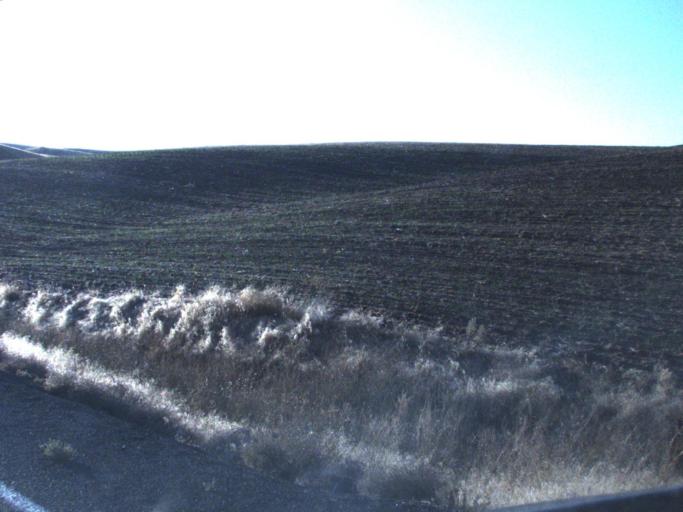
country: US
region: Washington
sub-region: Adams County
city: Ritzville
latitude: 46.6781
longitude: -118.3755
